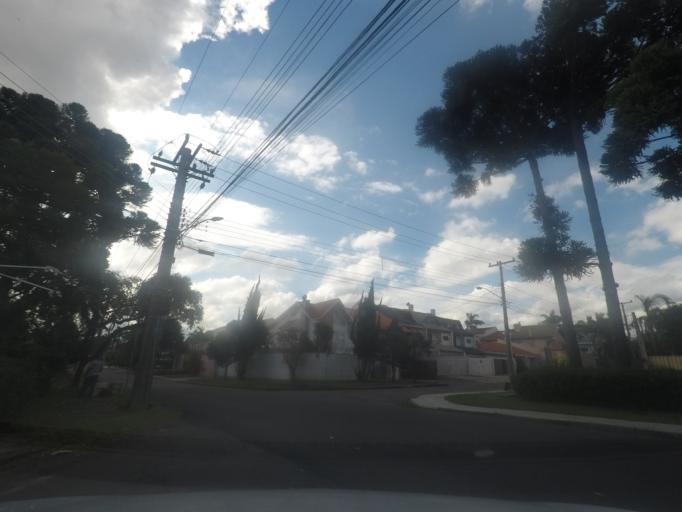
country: BR
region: Parana
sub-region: Pinhais
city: Pinhais
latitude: -25.4668
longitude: -49.2248
